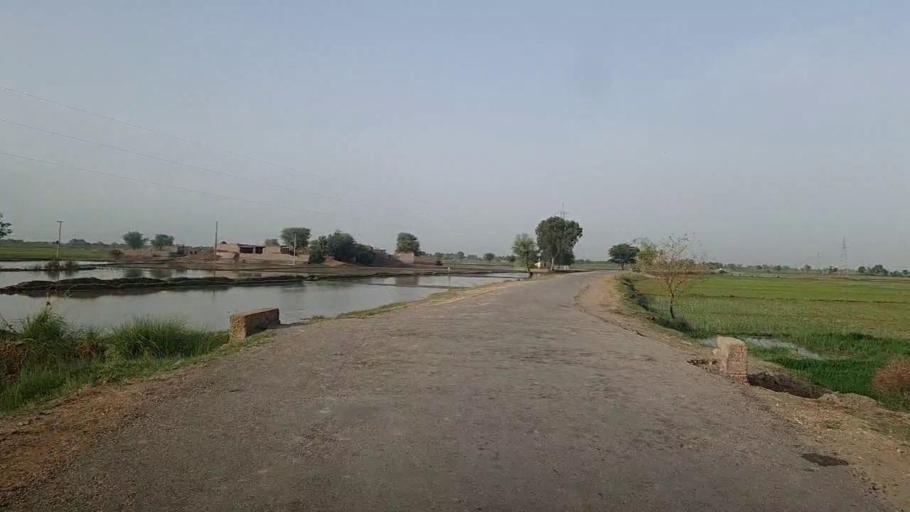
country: PK
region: Sindh
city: Mehar
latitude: 27.1437
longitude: 67.7956
